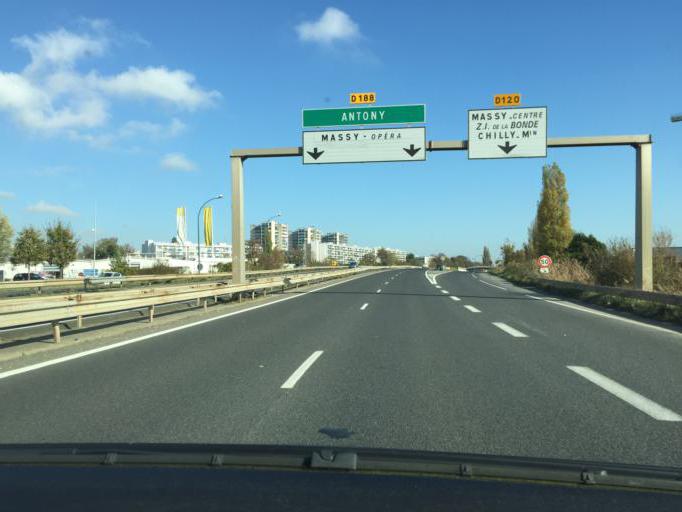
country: FR
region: Ile-de-France
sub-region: Departement de l'Essonne
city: Massy
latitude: 48.7243
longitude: 2.2795
